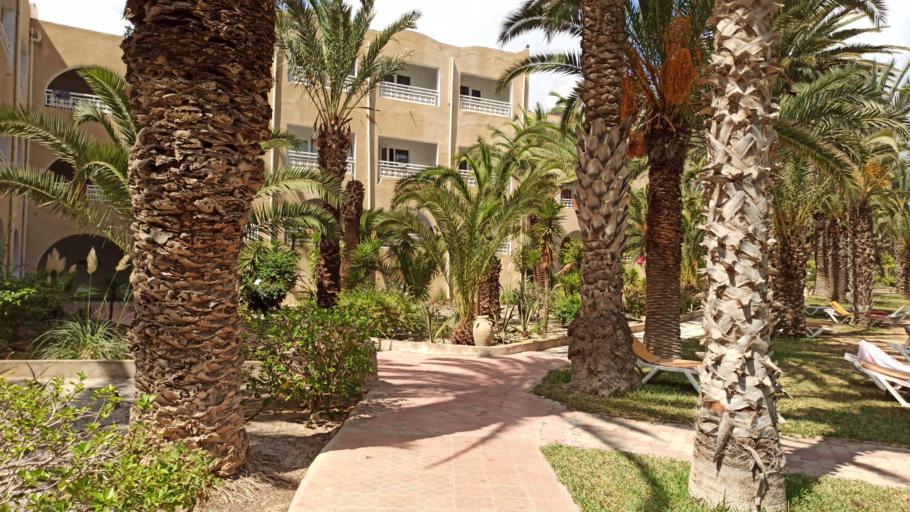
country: TN
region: Nabul
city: Al Hammamat
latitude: 36.4047
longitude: 10.6436
